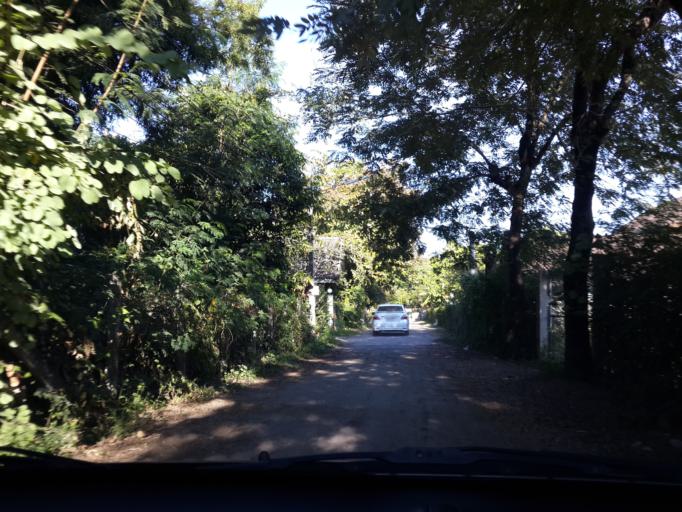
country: TH
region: Chiang Mai
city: Chiang Mai
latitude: 18.7441
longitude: 98.9451
